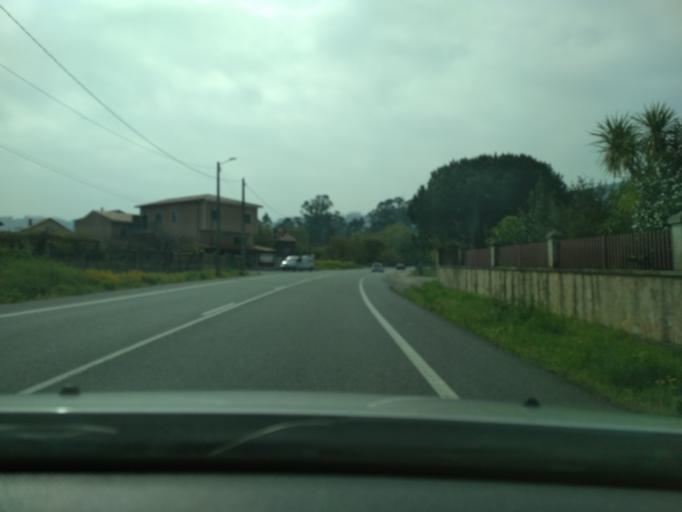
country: ES
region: Galicia
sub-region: Provincia de Pontevedra
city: Catoira
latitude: 42.6689
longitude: -8.7054
